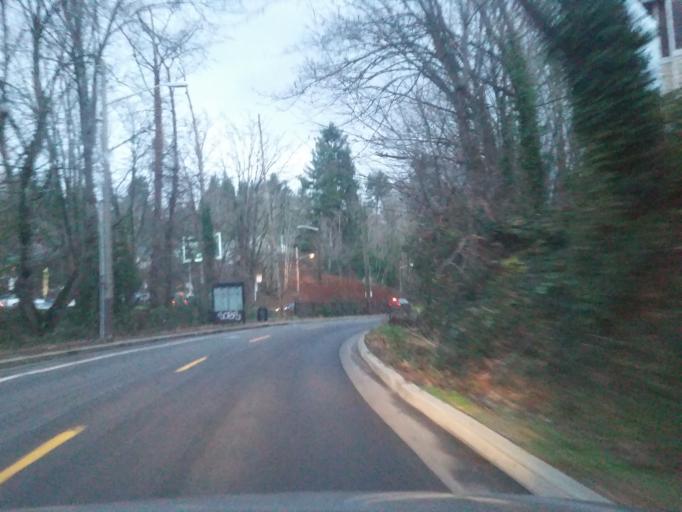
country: US
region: Washington
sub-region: King County
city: Lake Forest Park
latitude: 47.6950
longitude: -122.3048
